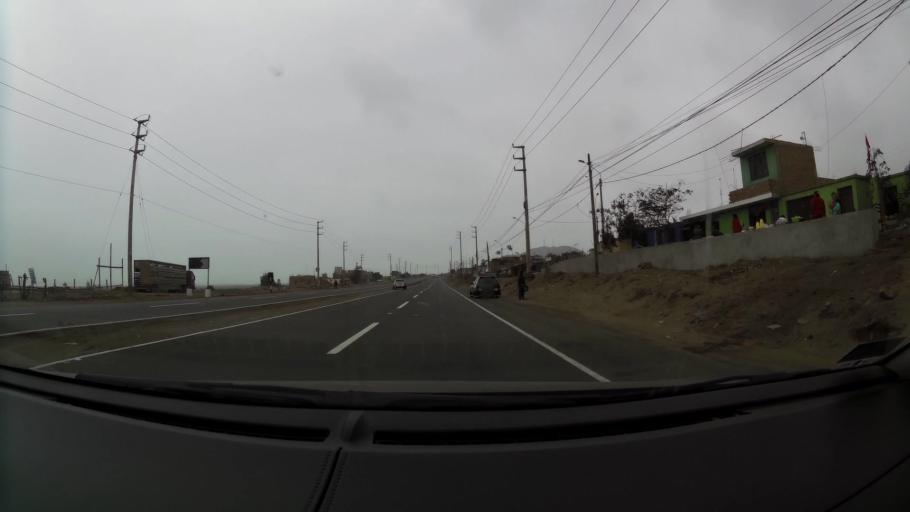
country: PE
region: Lima
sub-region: Provincia de Huaral
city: Chancay
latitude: -11.5984
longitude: -77.2509
